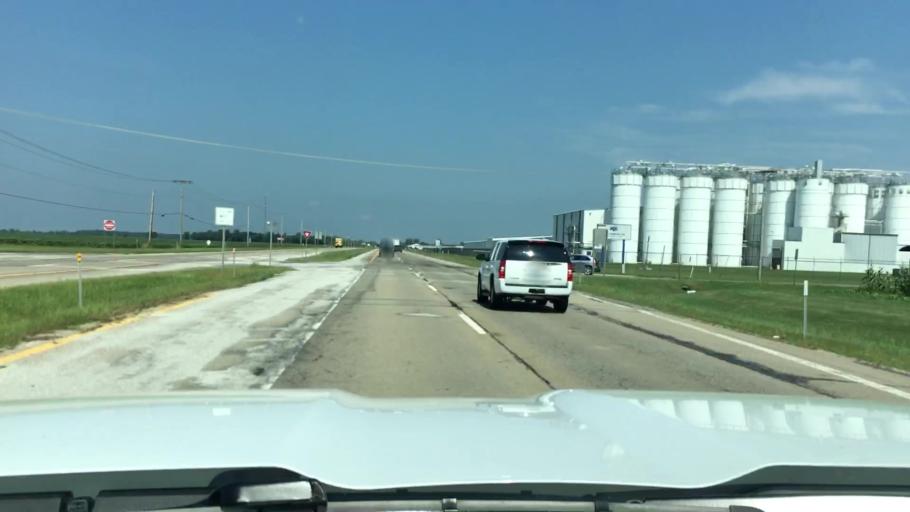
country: US
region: Michigan
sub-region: Kalamazoo County
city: Schoolcraft
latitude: 42.0771
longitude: -85.6365
